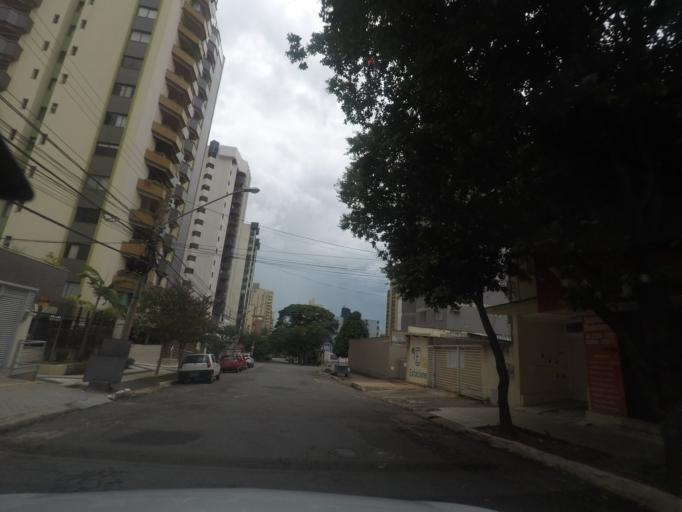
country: BR
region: Goias
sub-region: Goiania
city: Goiania
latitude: -16.6843
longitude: -49.2668
